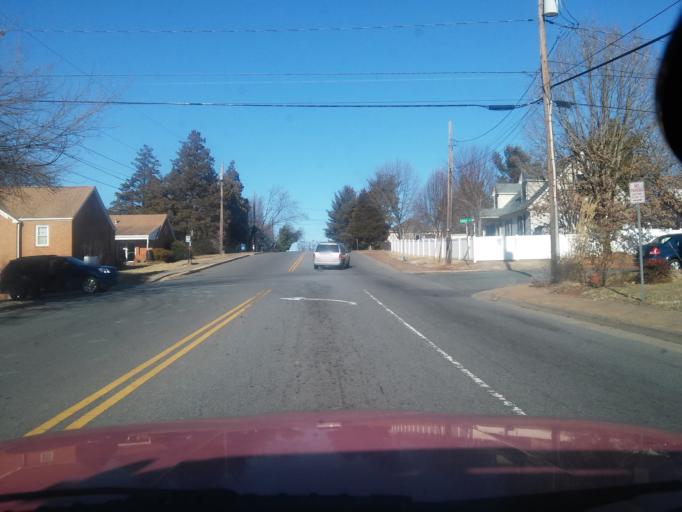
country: US
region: Virginia
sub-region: City of Charlottesville
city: Charlottesville
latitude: 38.0181
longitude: -78.4752
